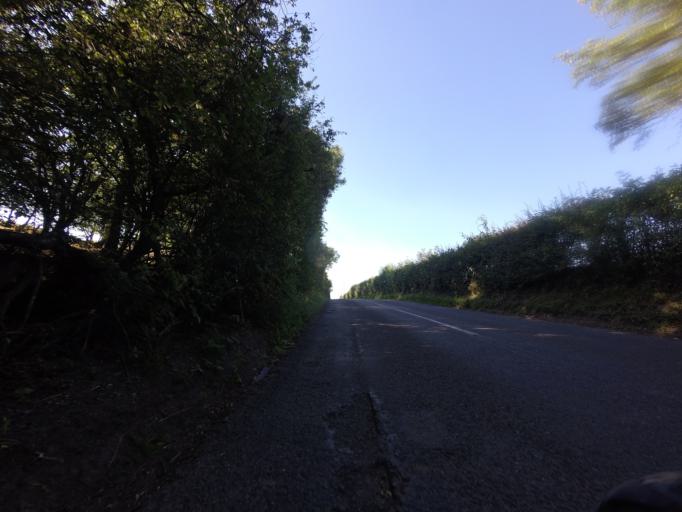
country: GB
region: England
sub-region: Kent
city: Tenterden
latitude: 51.0498
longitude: 0.6945
